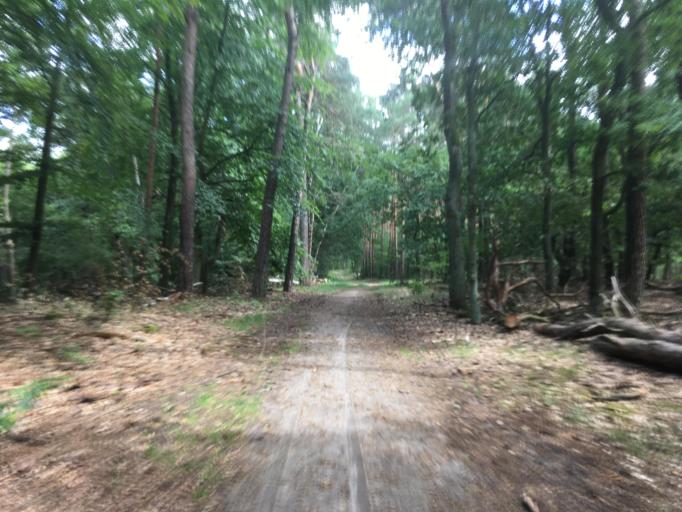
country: DE
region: Berlin
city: Friedrichshagen
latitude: 52.4265
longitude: 13.6105
